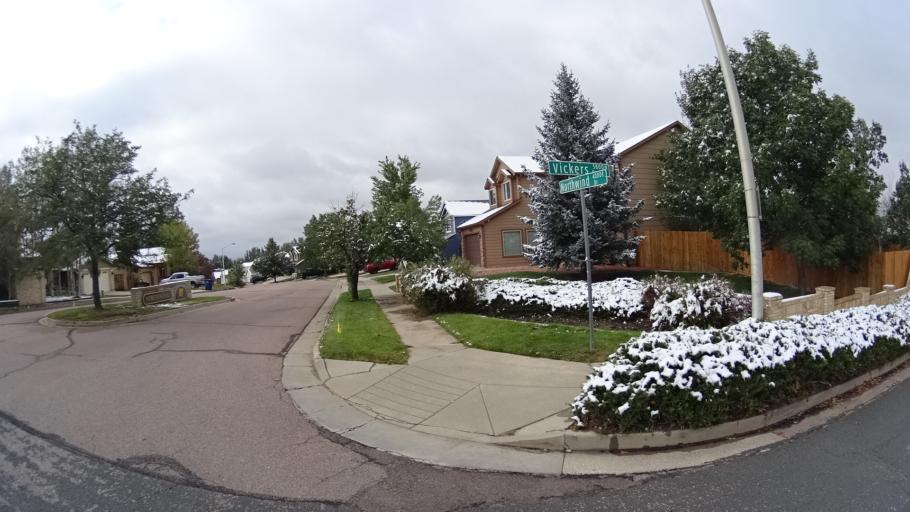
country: US
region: Colorado
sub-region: El Paso County
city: Cimarron Hills
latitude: 38.9172
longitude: -104.7540
